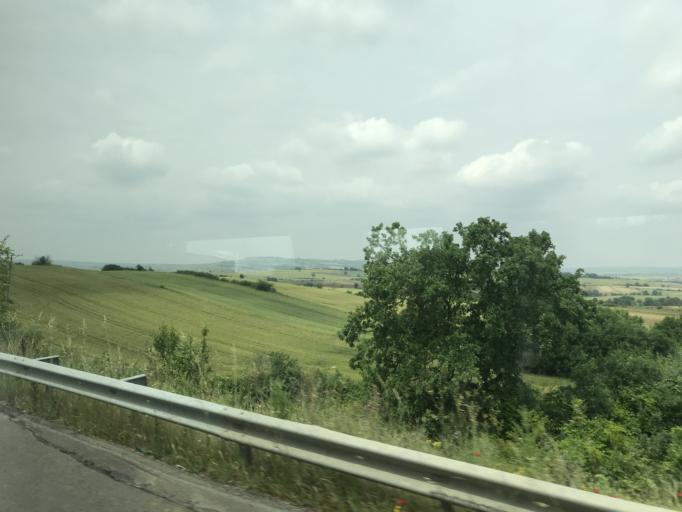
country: TR
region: Tekirdag
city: Inecik
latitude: 40.9348
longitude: 27.2562
